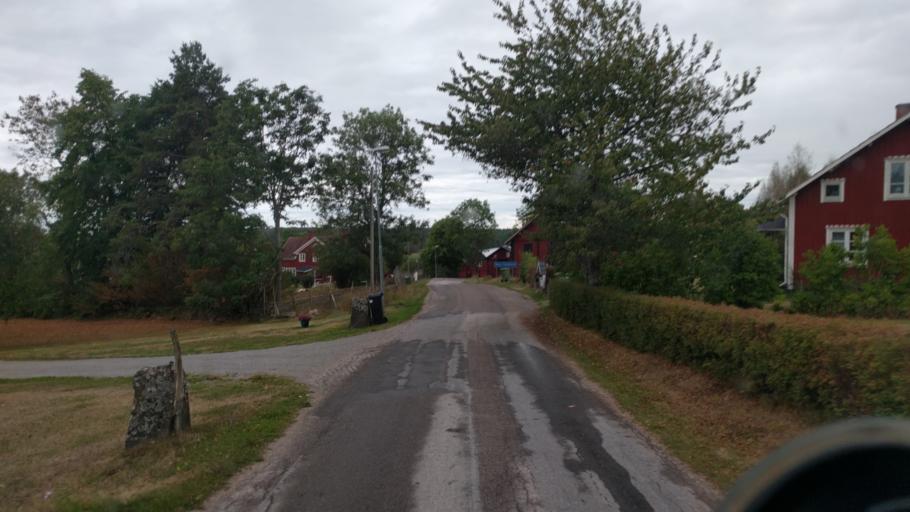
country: SE
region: Kalmar
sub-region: Vasterviks Kommun
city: Ankarsrum
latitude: 57.7442
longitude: 16.1738
